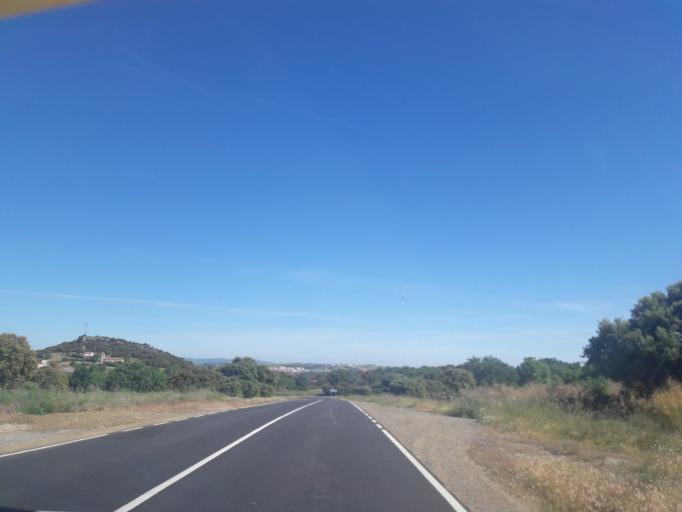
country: ES
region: Castille and Leon
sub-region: Provincia de Salamanca
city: Nava de Bejar
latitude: 40.4907
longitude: -5.6562
